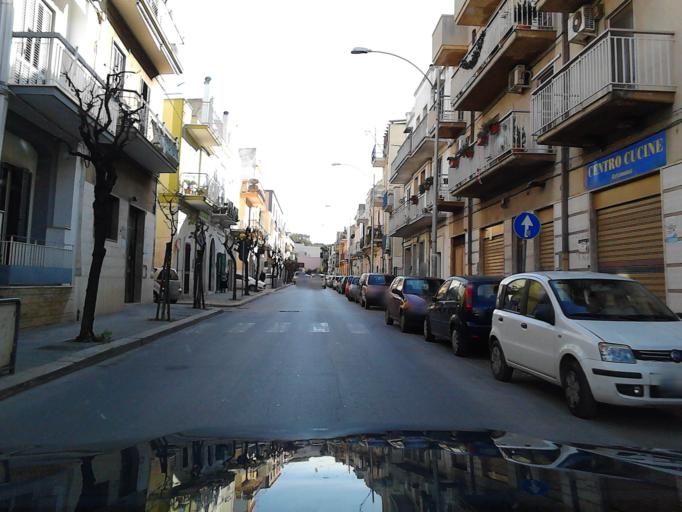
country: IT
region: Apulia
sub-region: Provincia di Bari
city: Rutigliano
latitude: 41.0138
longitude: 17.0017
